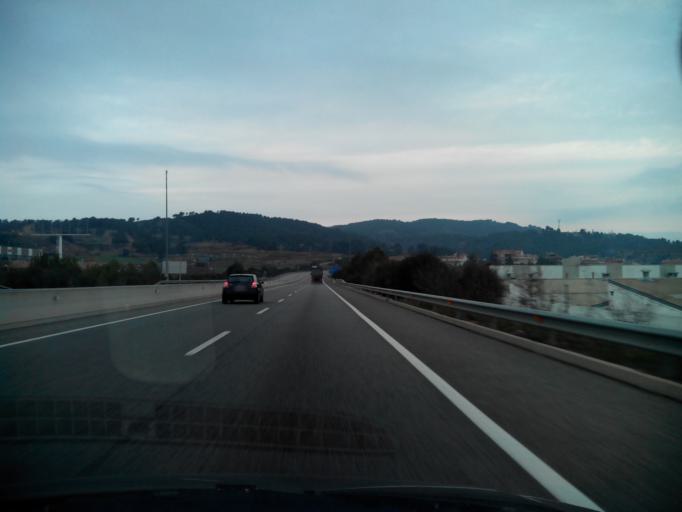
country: ES
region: Catalonia
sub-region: Provincia de Barcelona
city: Navas
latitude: 41.8942
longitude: 1.8715
